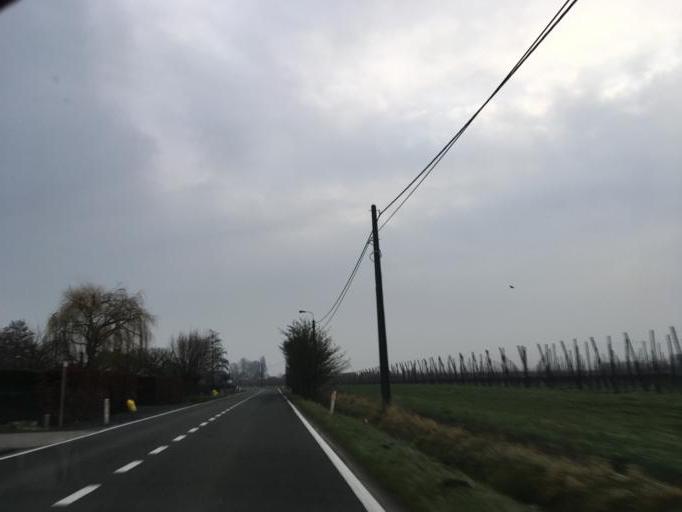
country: BE
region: Flanders
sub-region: Provincie West-Vlaanderen
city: Oostrozebeke
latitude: 50.9509
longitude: 3.3241
